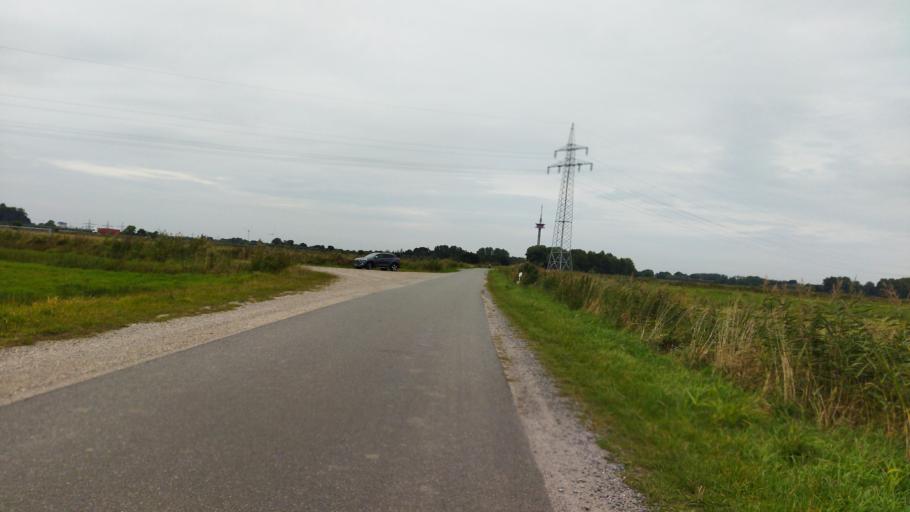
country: DE
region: Lower Saxony
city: Leer
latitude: 53.2504
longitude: 7.4381
